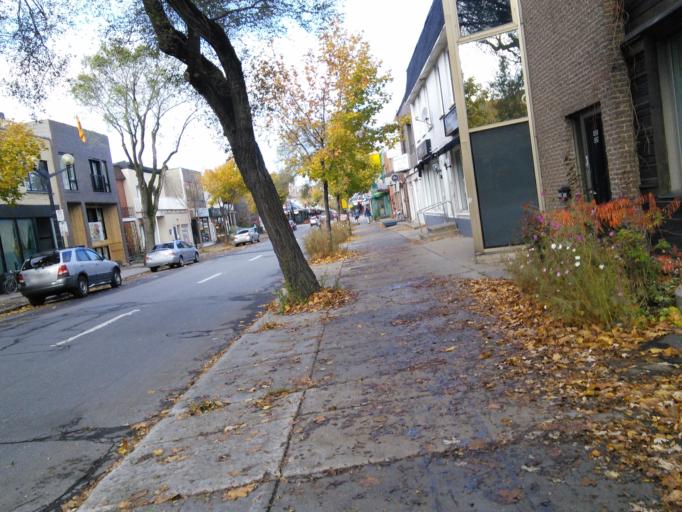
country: CA
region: Quebec
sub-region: Montreal
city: Montreal
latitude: 45.5341
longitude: -73.5987
